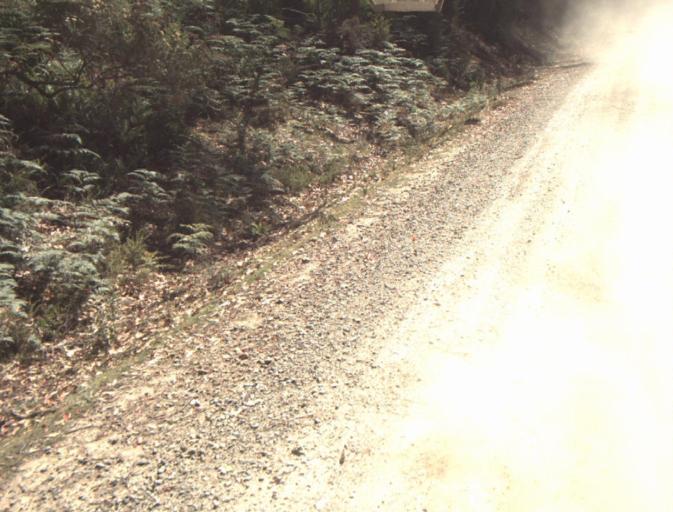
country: AU
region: Tasmania
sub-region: Dorset
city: Scottsdale
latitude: -41.3799
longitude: 147.4935
